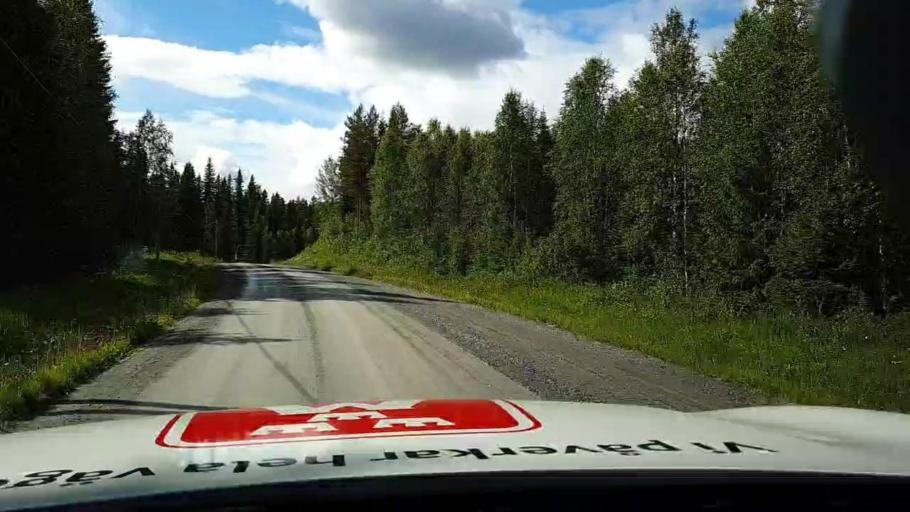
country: SE
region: Jaemtland
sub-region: Krokoms Kommun
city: Valla
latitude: 63.7109
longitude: 13.5431
